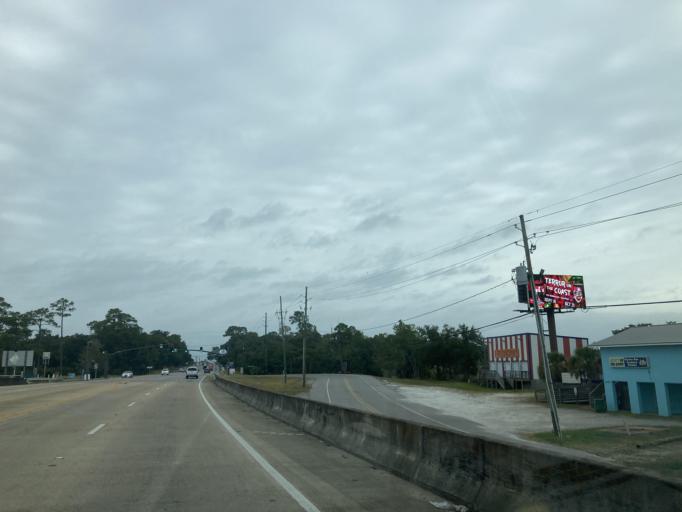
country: US
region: Mississippi
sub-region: Jackson County
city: Ocean Springs
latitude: 30.4224
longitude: -88.8288
